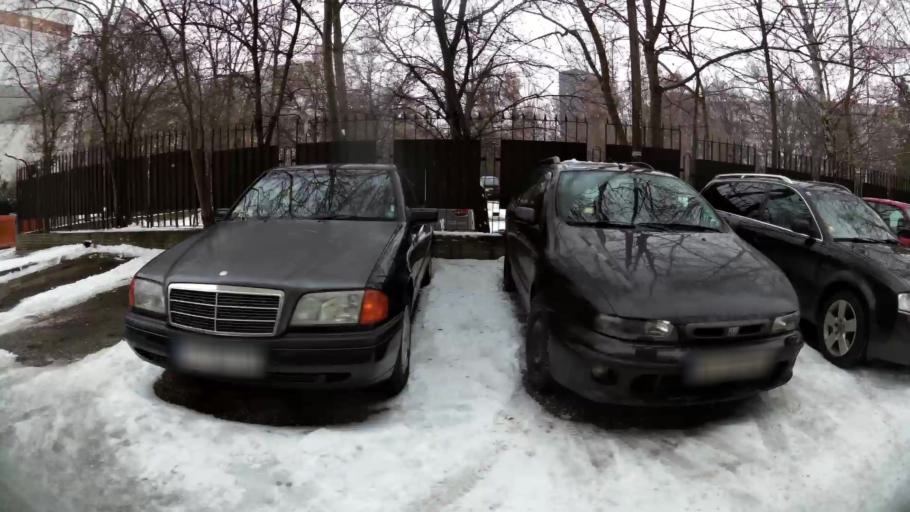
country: BG
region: Sofia-Capital
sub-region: Stolichna Obshtina
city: Sofia
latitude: 42.7121
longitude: 23.3115
